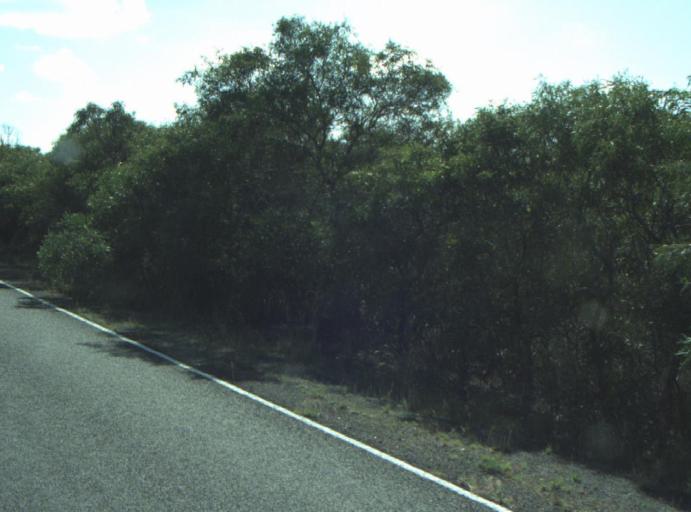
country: AU
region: Victoria
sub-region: Greater Geelong
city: Lara
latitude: -38.0104
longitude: 144.4283
